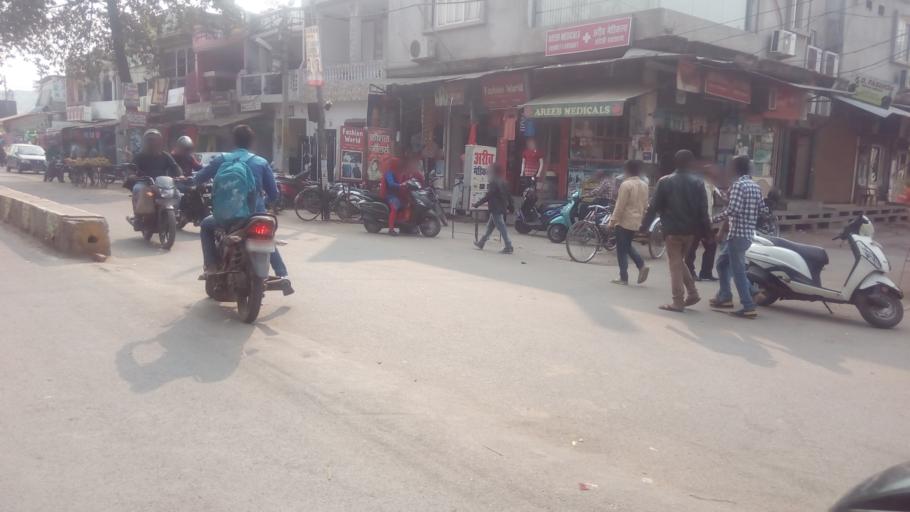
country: IN
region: Uttar Pradesh
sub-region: Lucknow District
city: Lucknow
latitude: 26.8427
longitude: 80.8769
